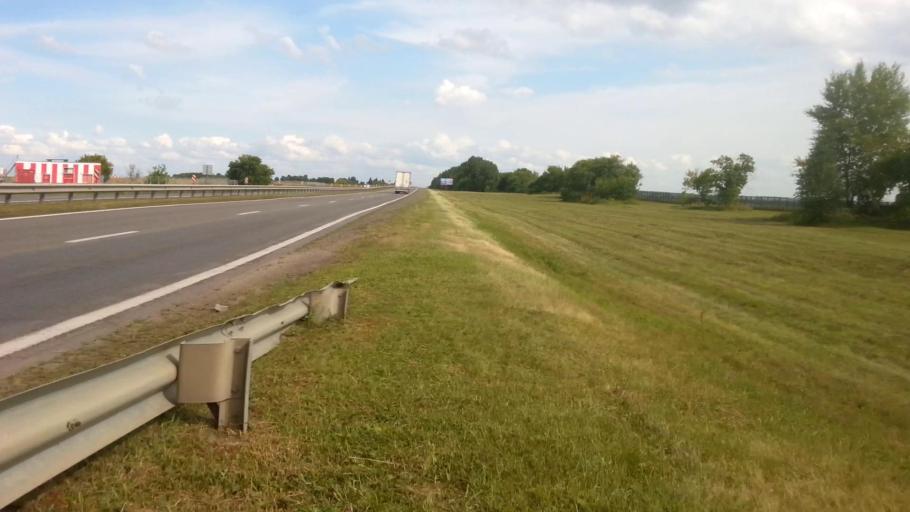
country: RU
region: Altai Krai
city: Nauchnyy Gorodok
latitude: 53.3563
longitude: 83.5118
